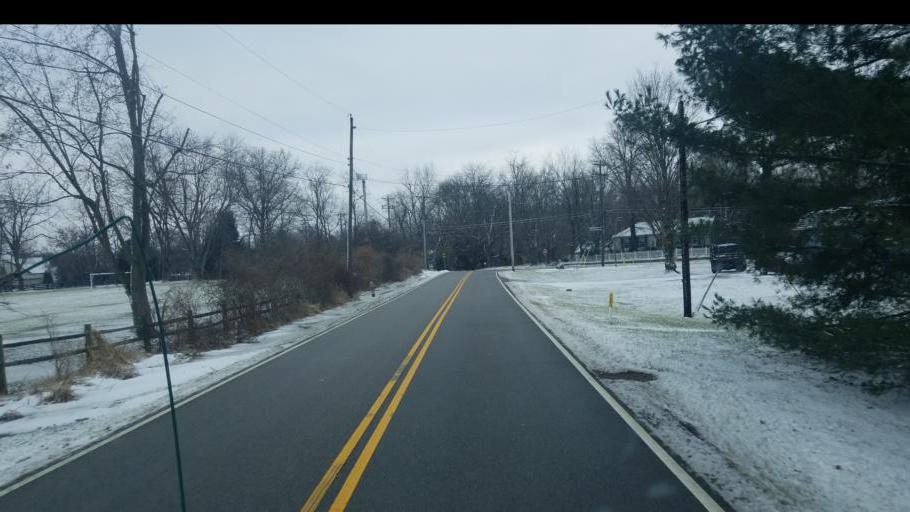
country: US
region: Ohio
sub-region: Franklin County
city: New Albany
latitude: 40.0425
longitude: -82.8240
